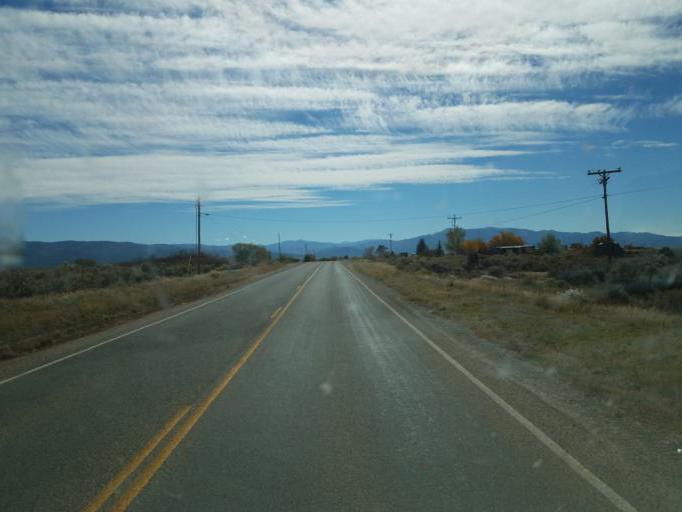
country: US
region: New Mexico
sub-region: Taos County
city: Taos Pueblo
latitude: 36.4656
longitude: -105.5936
